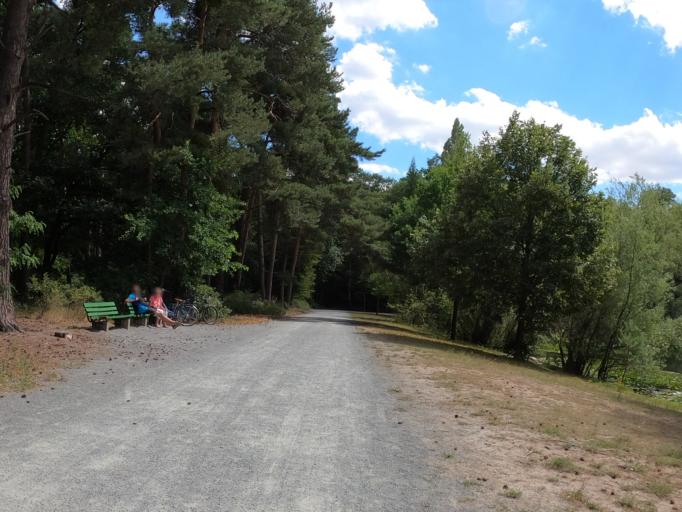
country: DE
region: Hesse
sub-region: Regierungsbezirk Darmstadt
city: Nauheim
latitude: 49.9688
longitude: 8.4644
